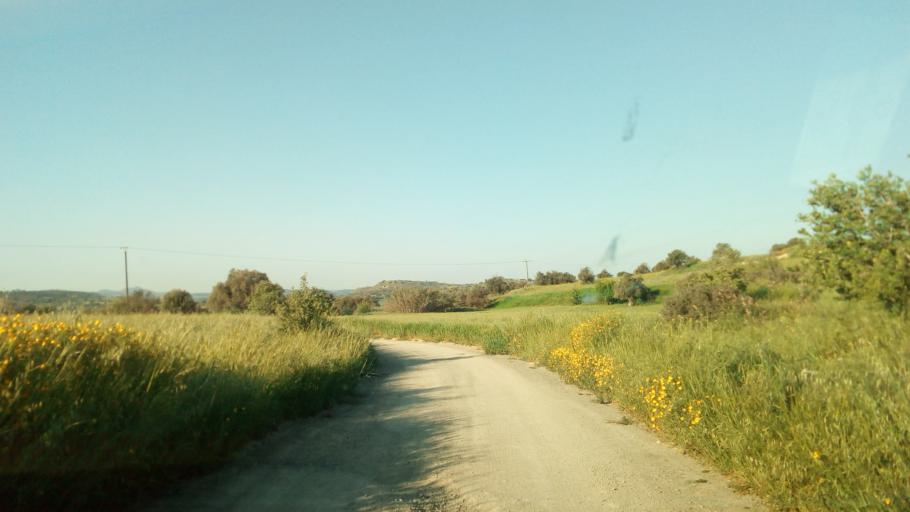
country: CY
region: Larnaka
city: Kofinou
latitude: 34.8373
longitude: 33.4519
